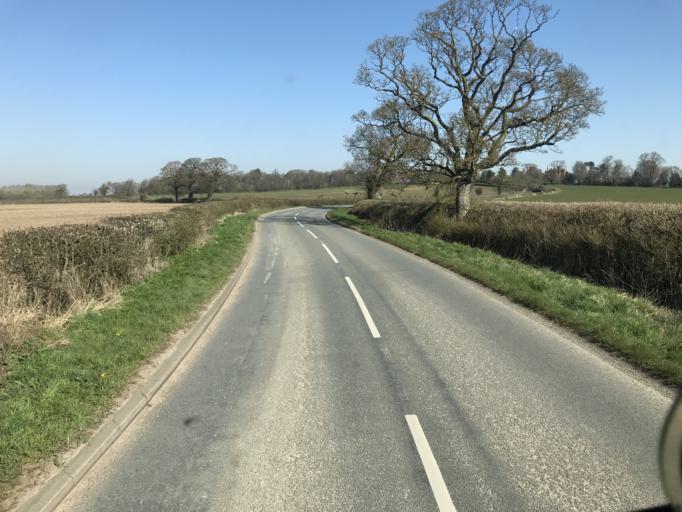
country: GB
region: England
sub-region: Cheshire West and Chester
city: Aldford
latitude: 53.1470
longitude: -2.8388
